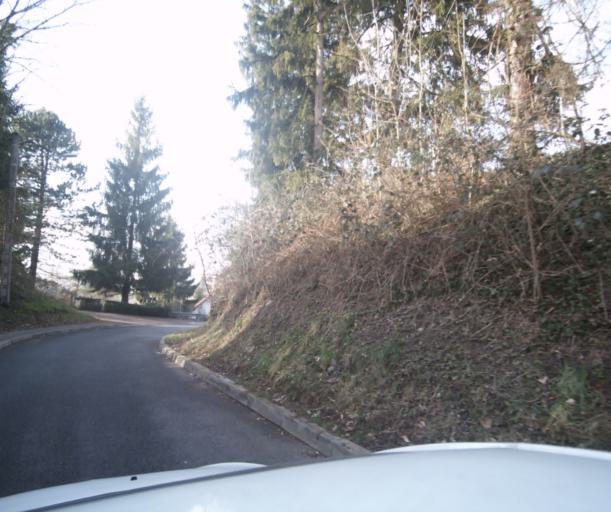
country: FR
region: Franche-Comte
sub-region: Departement du Doubs
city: Besancon
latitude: 47.2561
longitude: 6.0513
